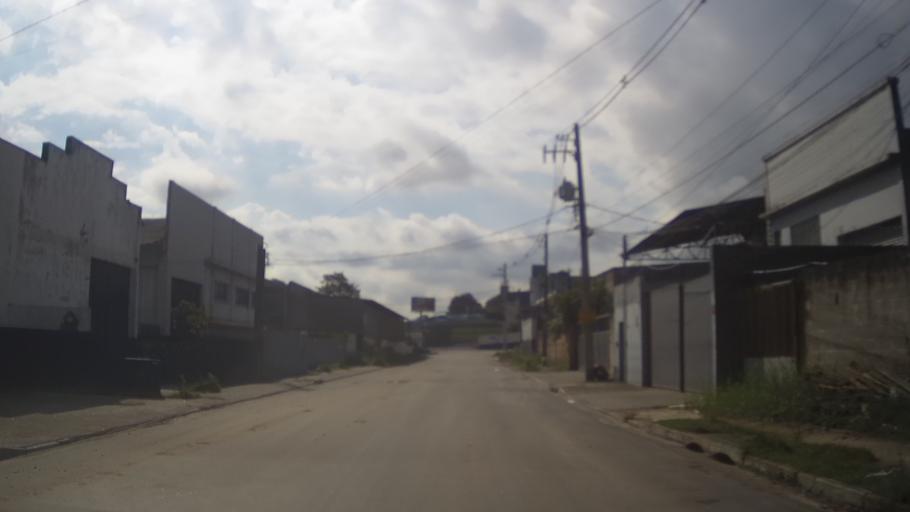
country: BR
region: Sao Paulo
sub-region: Guarulhos
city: Guarulhos
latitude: -23.4618
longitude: -46.4844
